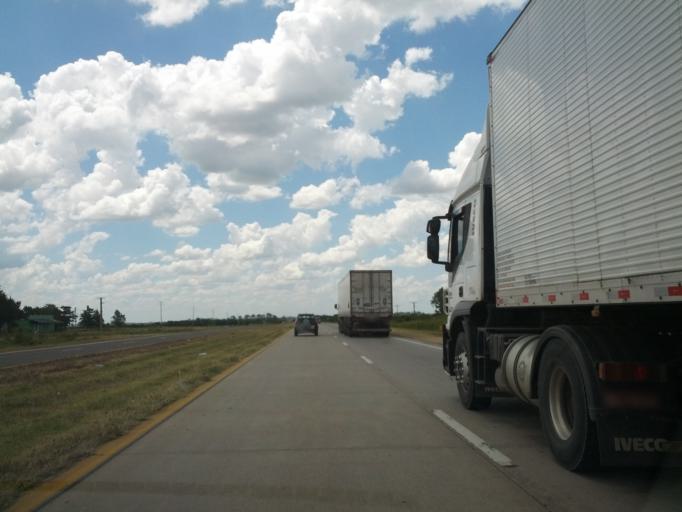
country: AR
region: Entre Rios
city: Gualeguaychu
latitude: -32.9962
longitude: -58.6002
